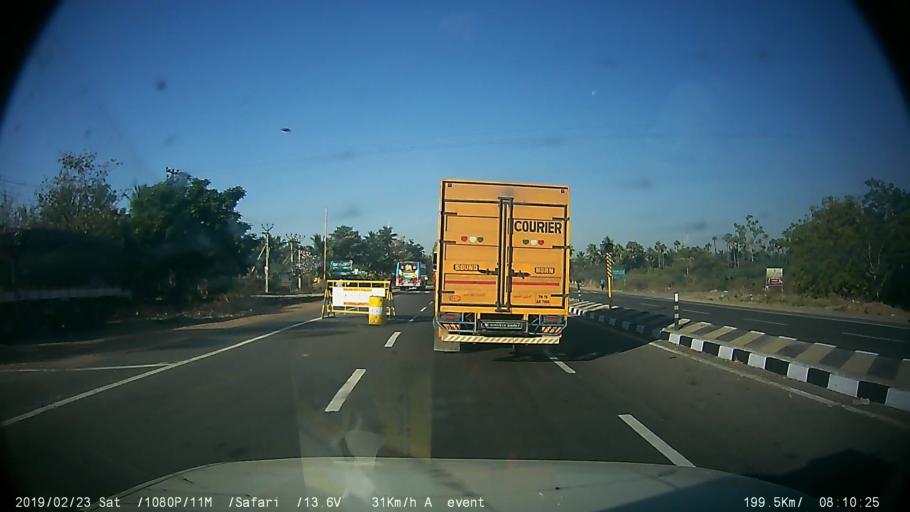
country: IN
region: Tamil Nadu
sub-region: Salem
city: Attayyampatti
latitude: 11.5605
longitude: 78.0190
